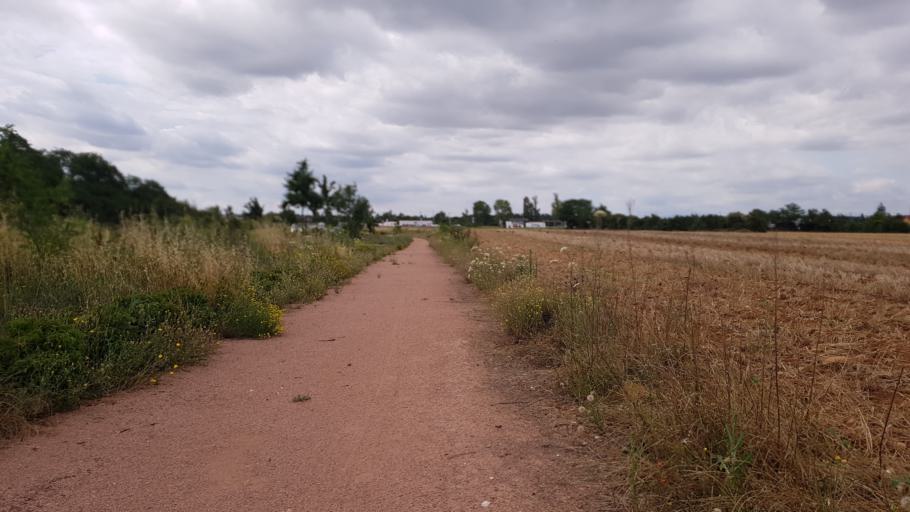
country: FR
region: Rhone-Alpes
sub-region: Departement du Rhone
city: Chassieu
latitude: 45.7214
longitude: 4.9554
